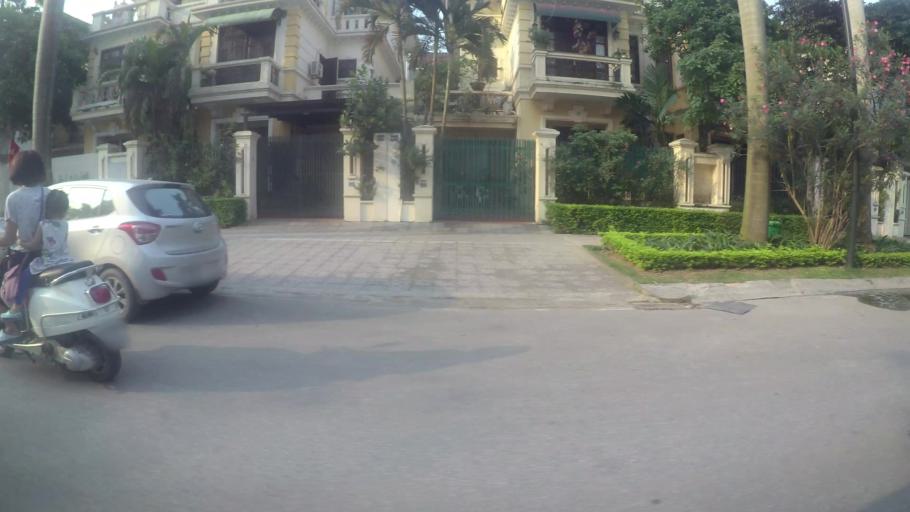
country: VN
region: Ha Noi
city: Tay Ho
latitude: 21.0747
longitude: 105.8015
